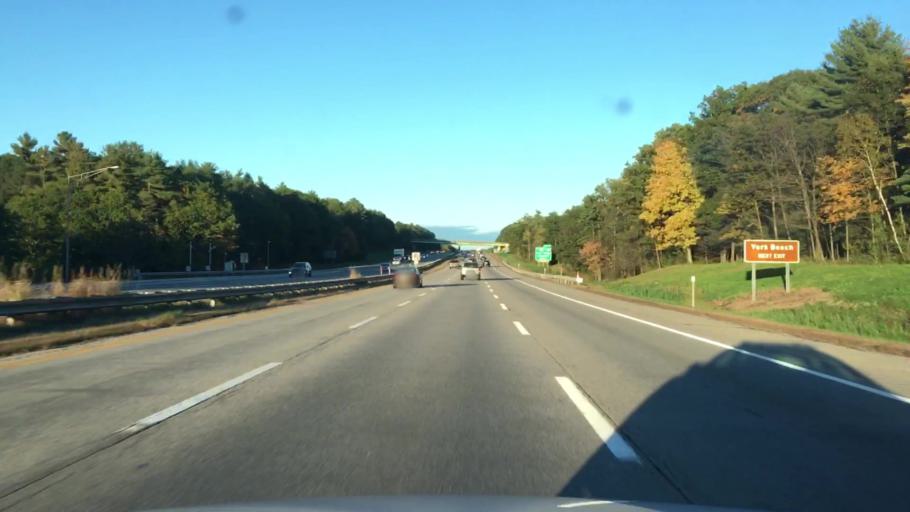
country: US
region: Maine
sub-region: York County
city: Kittery Point
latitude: 43.1377
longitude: -70.7056
